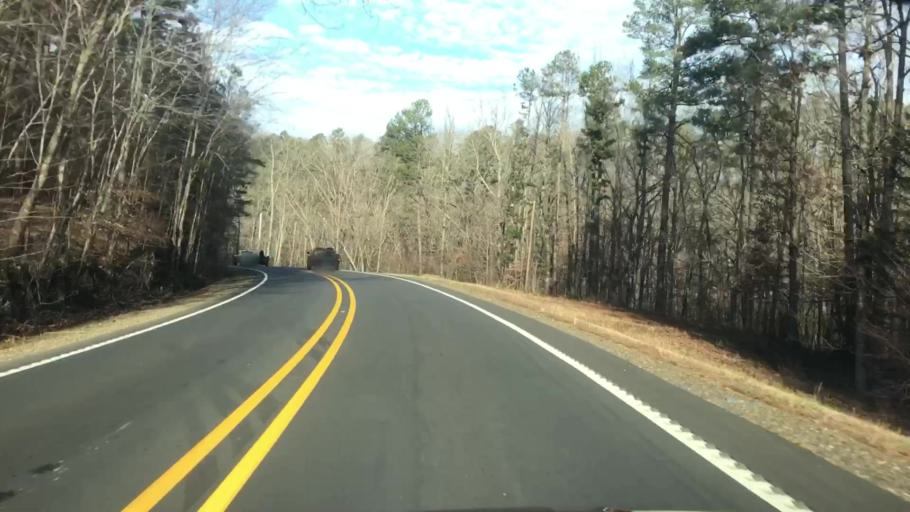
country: US
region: Arkansas
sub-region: Montgomery County
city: Mount Ida
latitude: 34.5240
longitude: -93.4010
